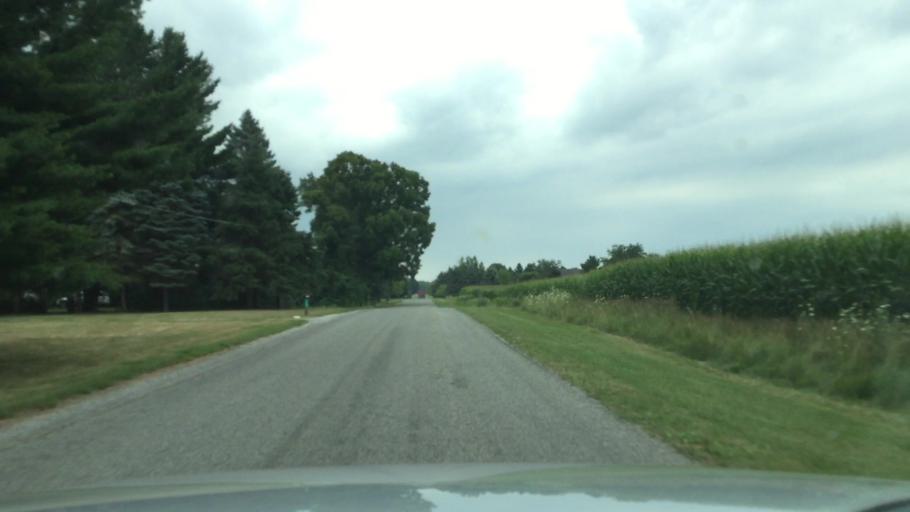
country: US
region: Michigan
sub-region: Saginaw County
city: Frankenmuth
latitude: 43.3159
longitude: -83.7957
